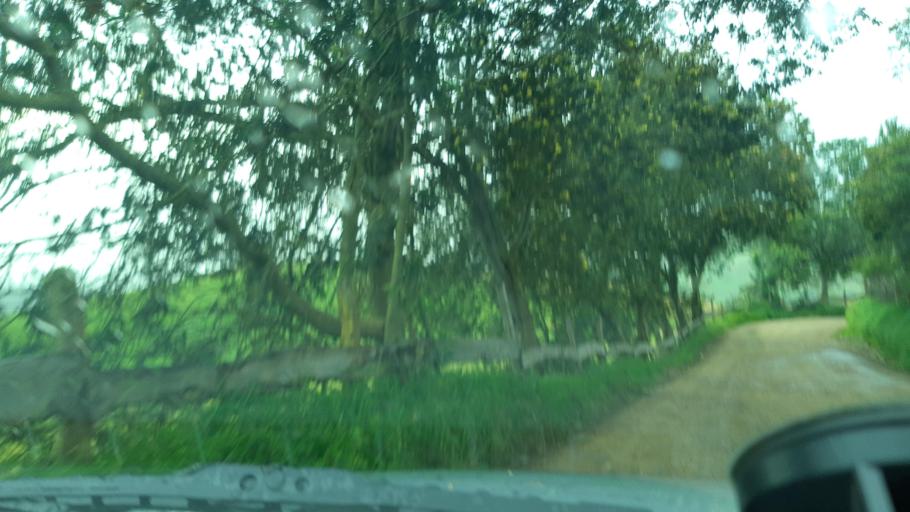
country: CO
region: Cundinamarca
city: Villapinzon
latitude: 5.2284
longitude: -73.5827
